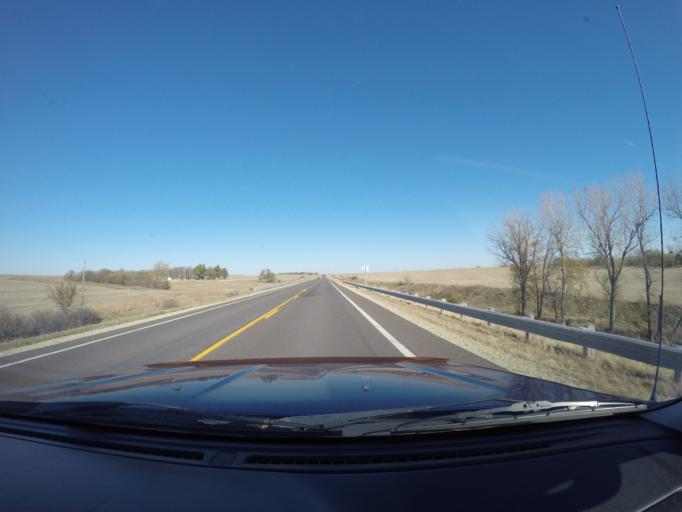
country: US
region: Kansas
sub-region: Marshall County
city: Blue Rapids
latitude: 39.5448
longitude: -96.7553
